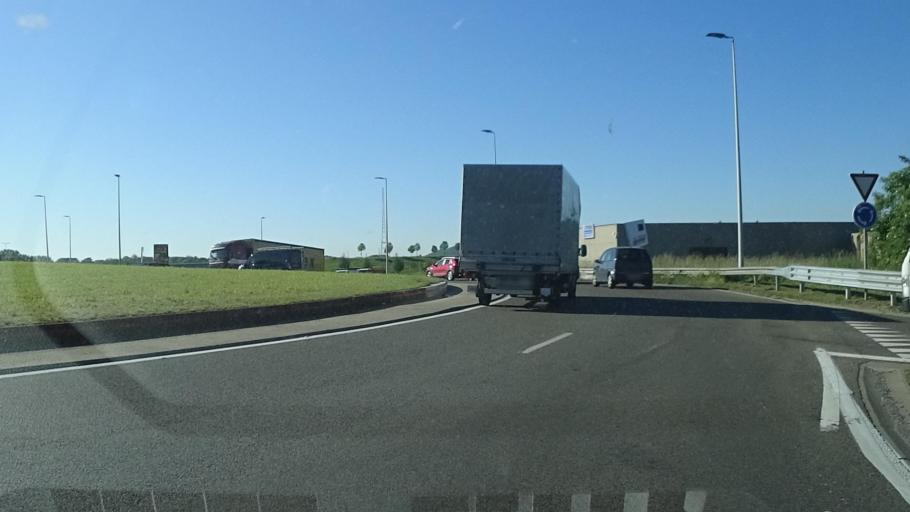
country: BE
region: Wallonia
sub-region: Province du Hainaut
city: Roeulx
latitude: 50.4957
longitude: 4.1303
